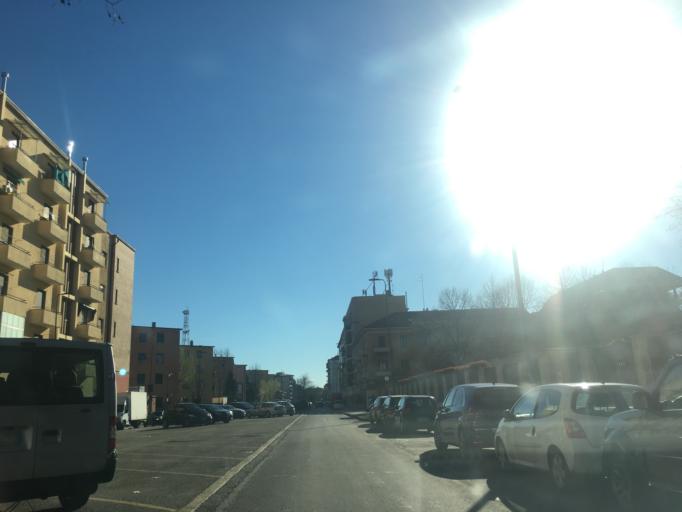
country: IT
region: Lombardy
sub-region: Citta metropolitana di Milano
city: Romano Banco
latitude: 45.4747
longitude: 9.1359
